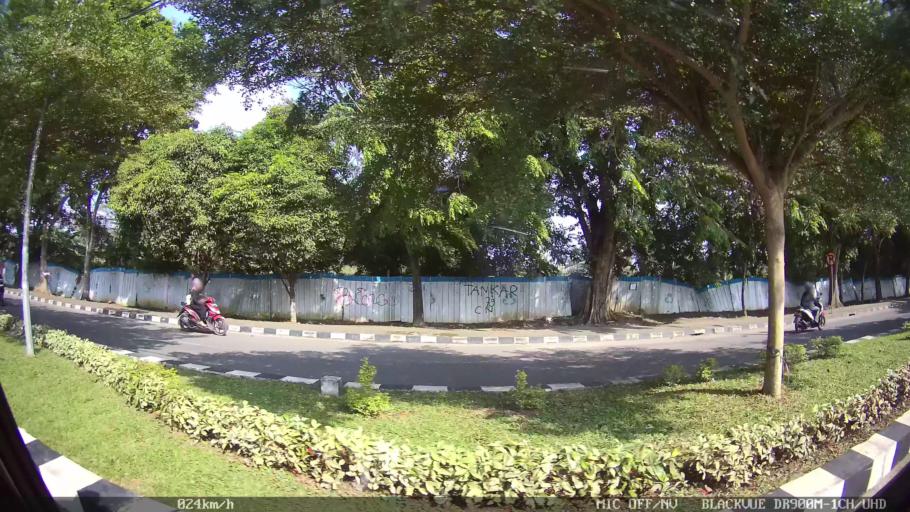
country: ID
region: Lampung
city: Kedaton
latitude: -5.3702
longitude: 105.2406
